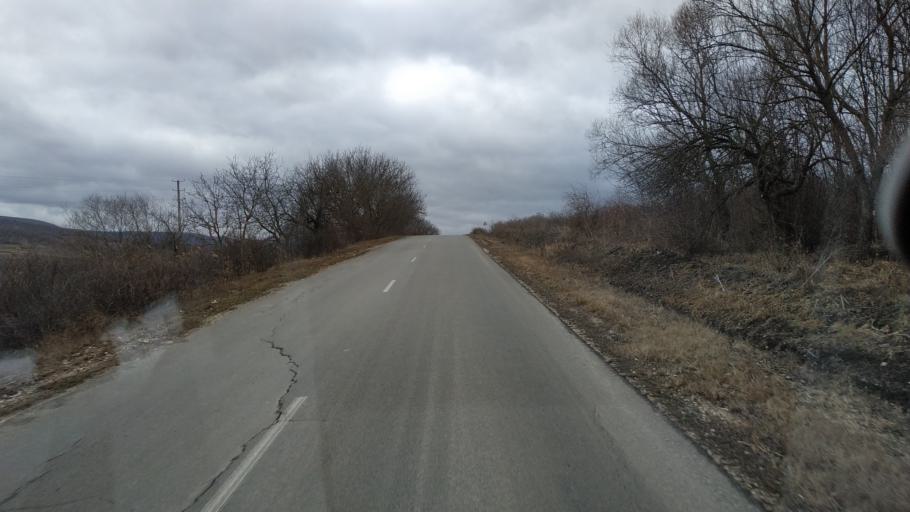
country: MD
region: Calarasi
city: Calarasi
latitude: 47.2399
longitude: 28.1678
